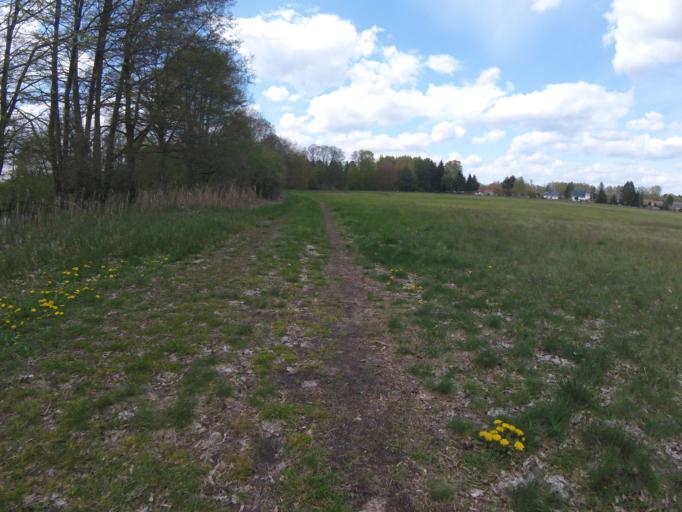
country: DE
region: Brandenburg
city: Munchehofe
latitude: 52.2191
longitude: 13.7709
